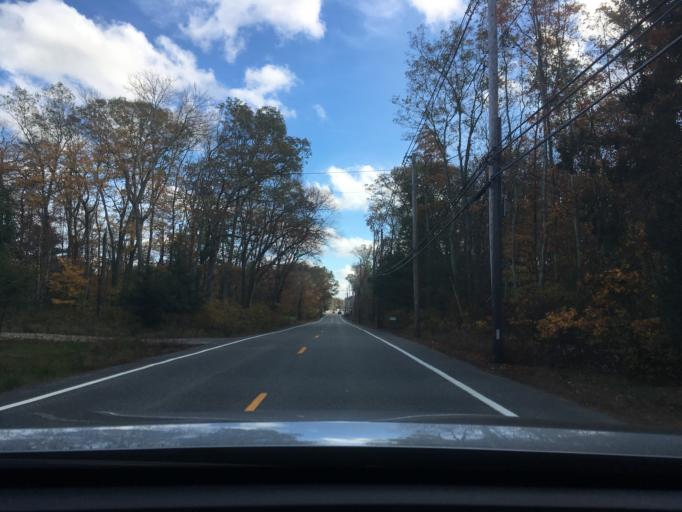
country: US
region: Rhode Island
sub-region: Providence County
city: Chepachet
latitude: 41.8305
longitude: -71.6729
